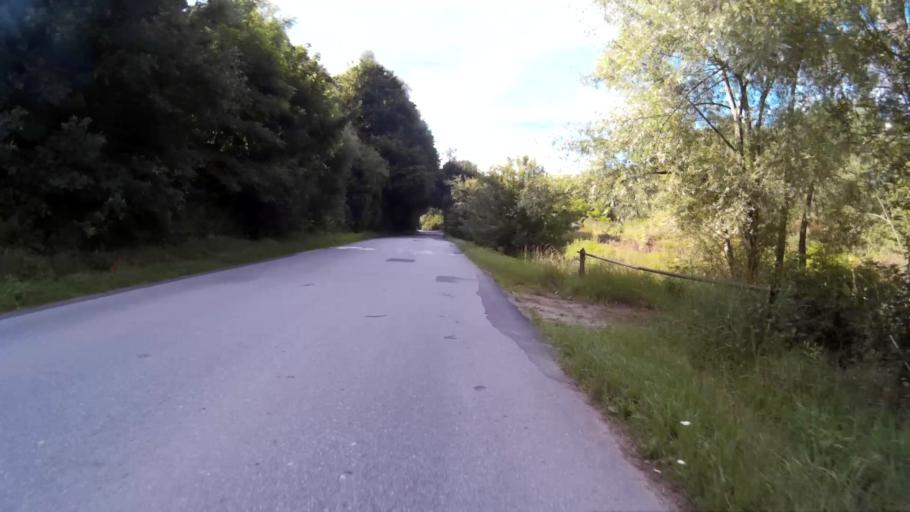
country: CZ
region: South Moravian
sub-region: Okres Brno-Venkov
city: Rosice
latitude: 49.1684
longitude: 16.4192
